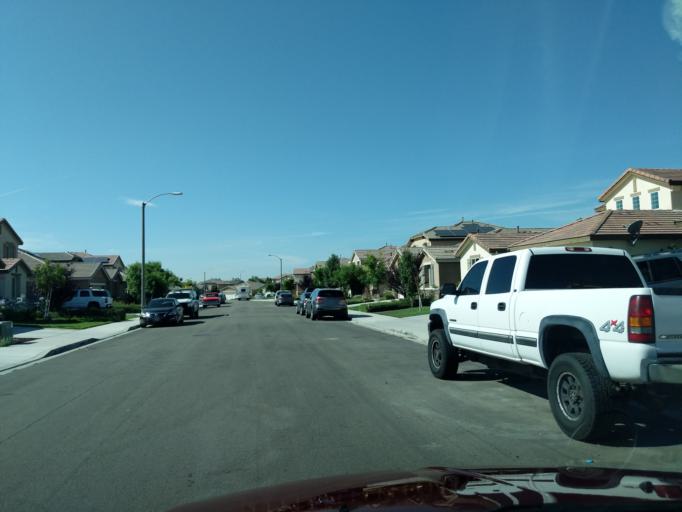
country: US
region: California
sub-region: San Bernardino County
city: Muscoy
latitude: 34.1869
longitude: -117.4164
